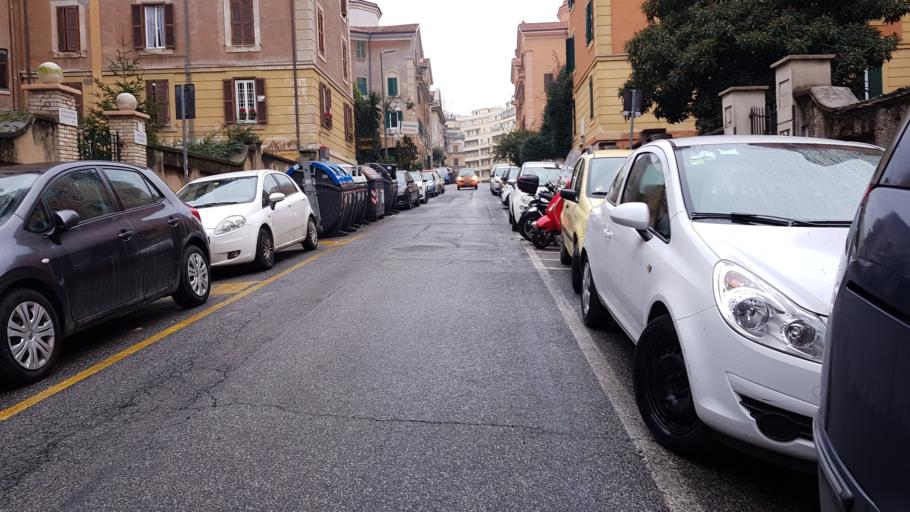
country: IT
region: Latium
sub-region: Citta metropolitana di Roma Capitale
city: Rome
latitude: 41.9099
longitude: 12.5252
